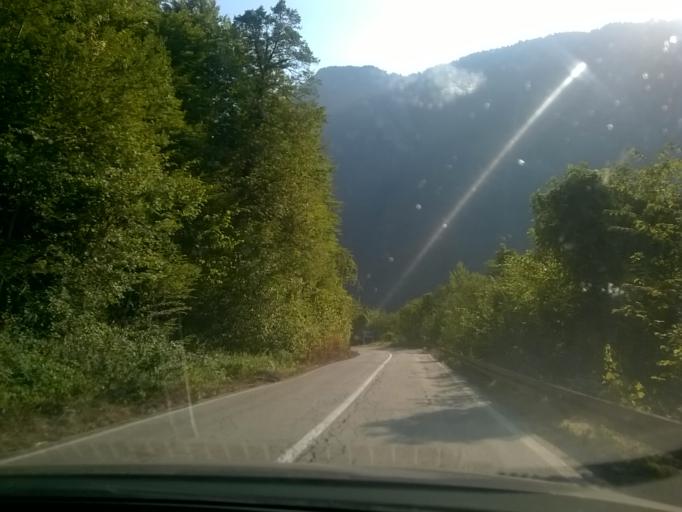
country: ME
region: Opstina Pluzine
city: Pluzine
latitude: 43.3107
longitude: 18.8533
